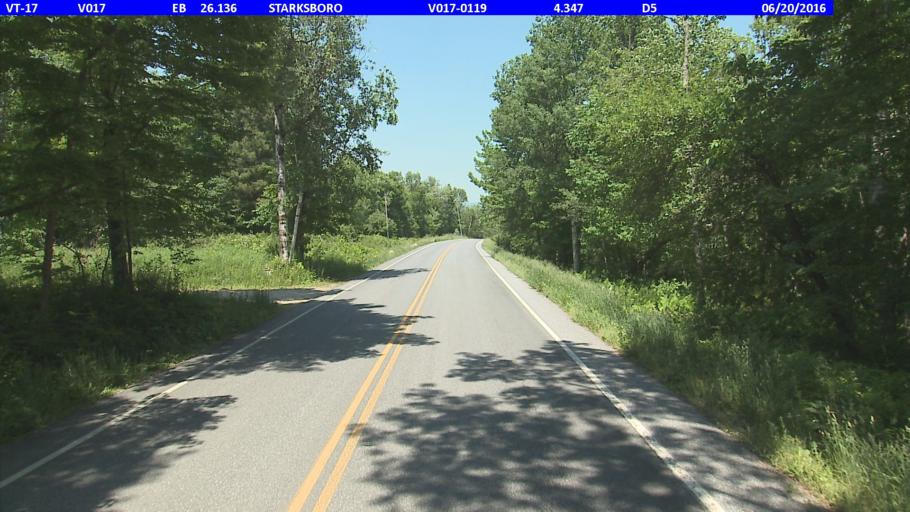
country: US
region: Vermont
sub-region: Addison County
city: Bristol
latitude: 44.2017
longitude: -72.9650
